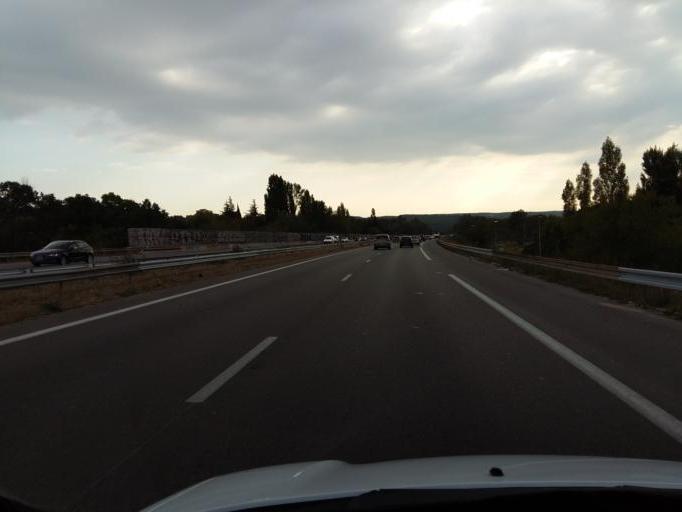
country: FR
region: Provence-Alpes-Cote d'Azur
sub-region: Departement des Bouches-du-Rhone
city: Bouc-Bel-Air
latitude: 43.4607
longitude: 5.4046
